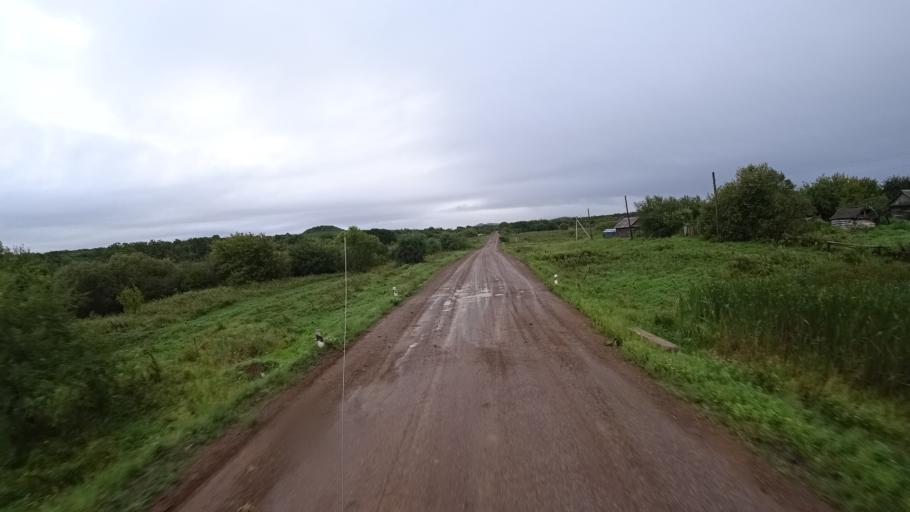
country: RU
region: Primorskiy
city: Monastyrishche
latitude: 44.2765
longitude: 132.4262
